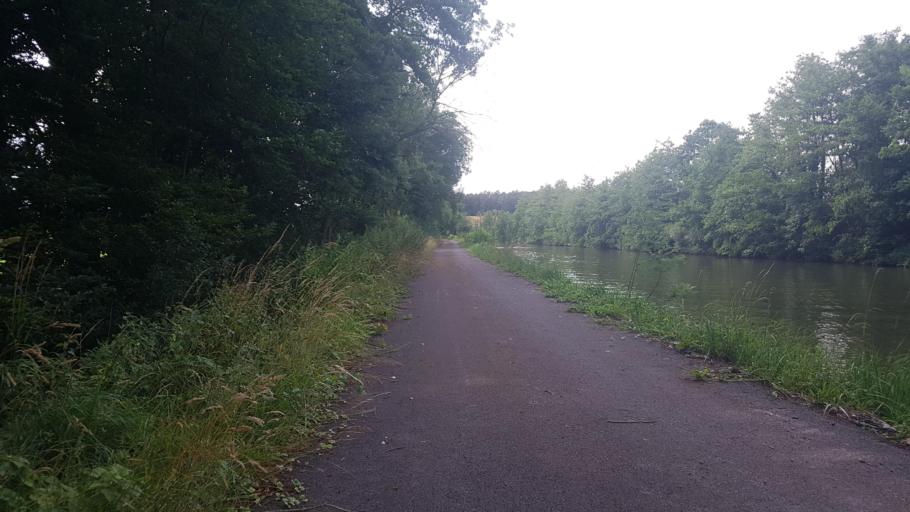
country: FR
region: Lorraine
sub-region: Departement de la Moselle
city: Dieuze
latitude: 48.6967
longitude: 6.7427
